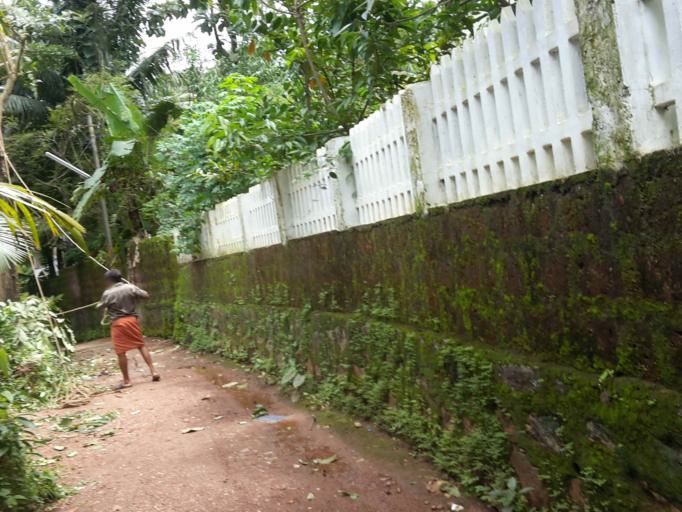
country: IN
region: Kerala
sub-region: Kozhikode
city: Kozhikode
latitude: 11.2840
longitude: 75.7950
